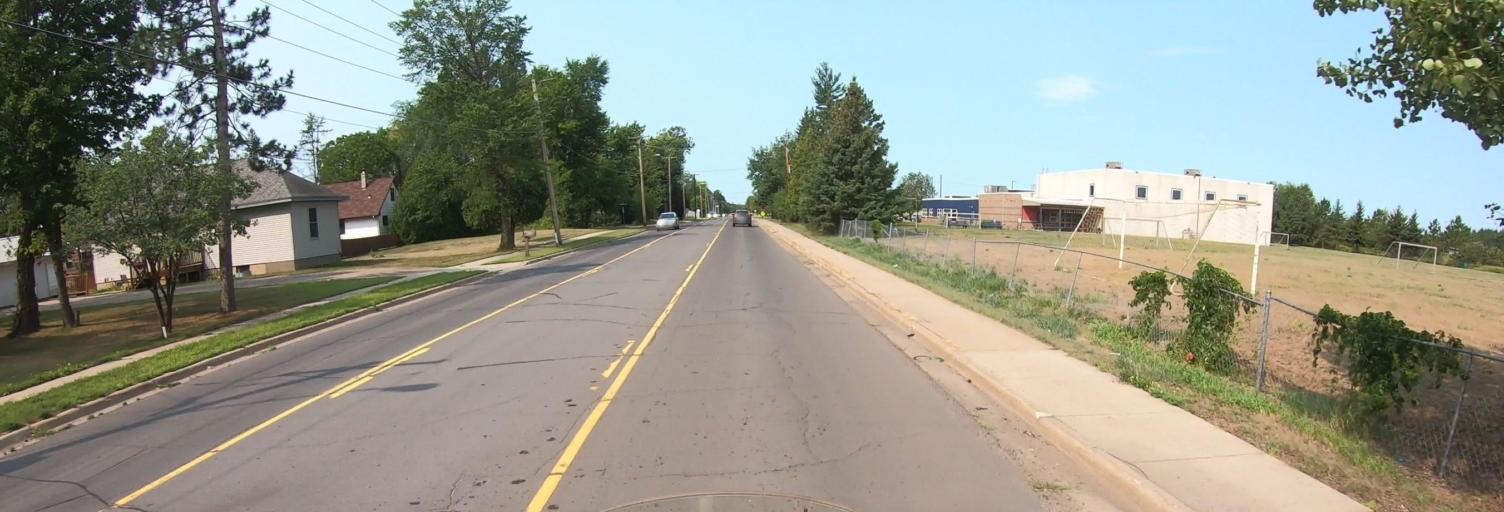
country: US
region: Minnesota
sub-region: Saint Louis County
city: Parkville
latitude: 47.5175
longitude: -92.5650
